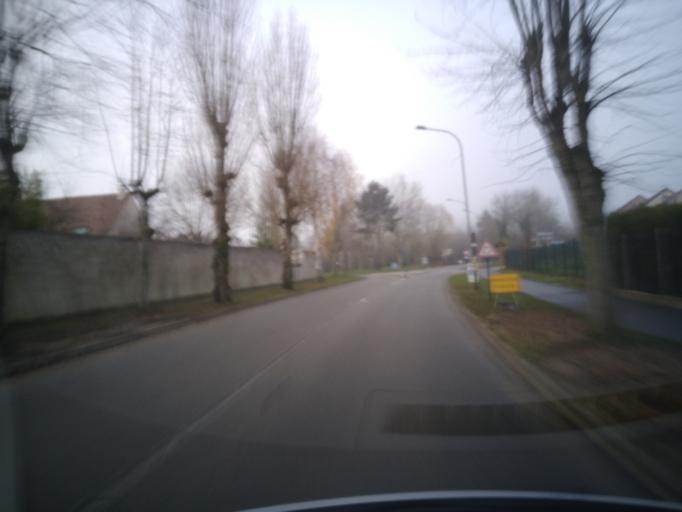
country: FR
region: Ile-de-France
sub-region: Departement des Yvelines
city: Orgeval
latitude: 48.9181
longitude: 1.9671
